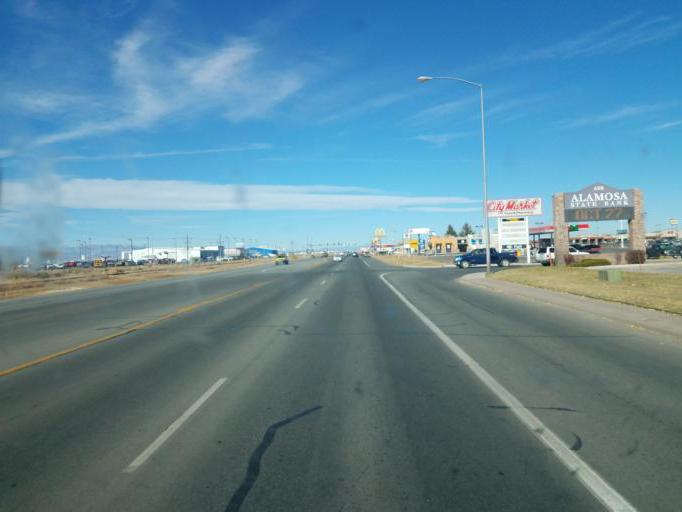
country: US
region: Colorado
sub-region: Alamosa County
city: Alamosa
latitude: 37.4739
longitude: -105.8916
